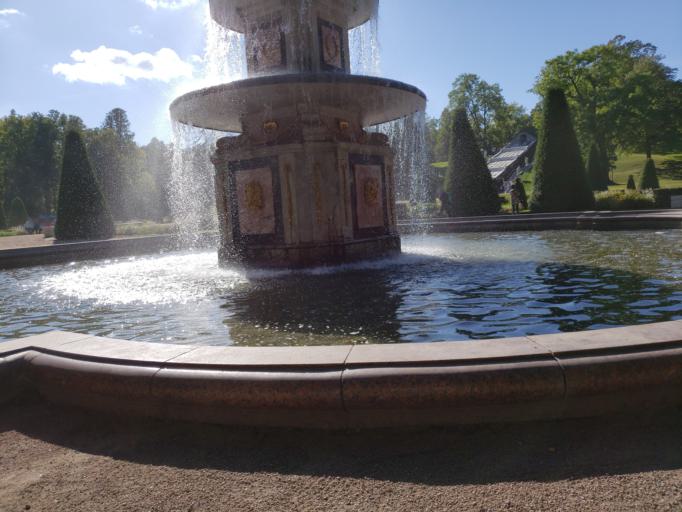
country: RU
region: St.-Petersburg
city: Peterhof
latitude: 59.8843
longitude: 29.9165
